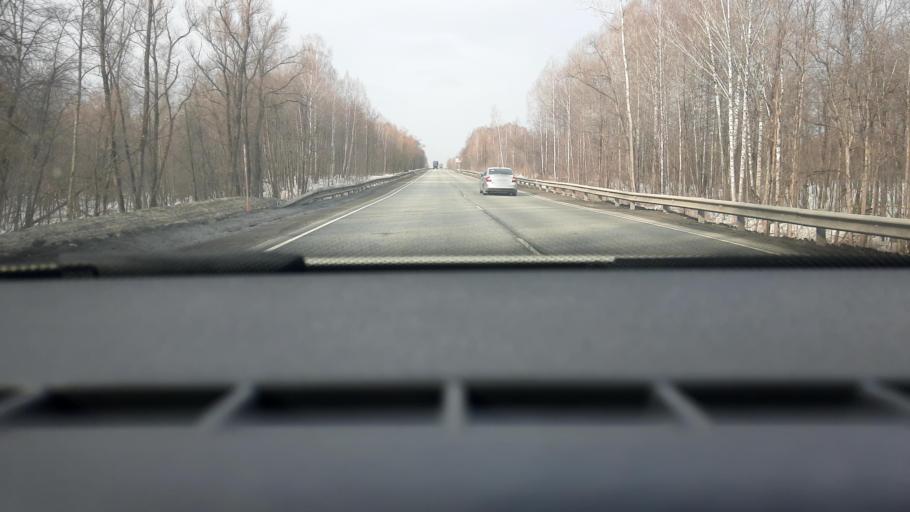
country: RU
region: Chelyabinsk
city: Asha
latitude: 54.8848
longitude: 57.2806
